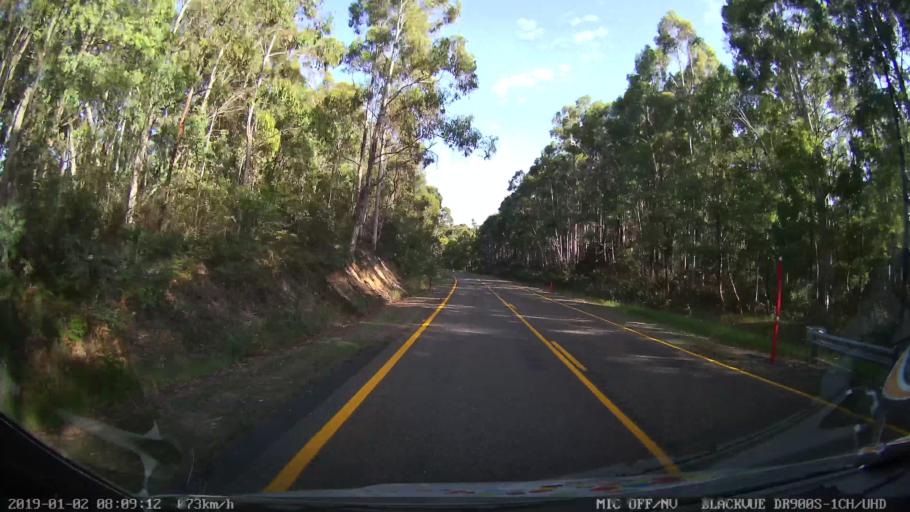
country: AU
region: New South Wales
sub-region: Tumut Shire
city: Tumut
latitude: -35.6093
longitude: 148.3809
